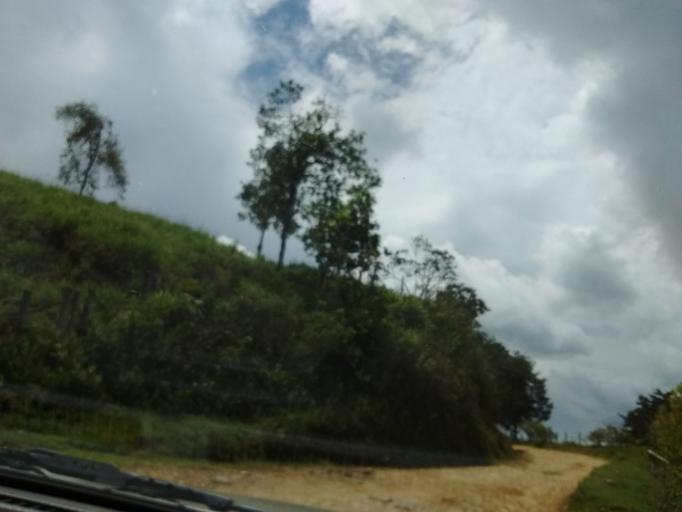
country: CO
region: Cauca
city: Villa Rica
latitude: 2.5975
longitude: -76.7593
